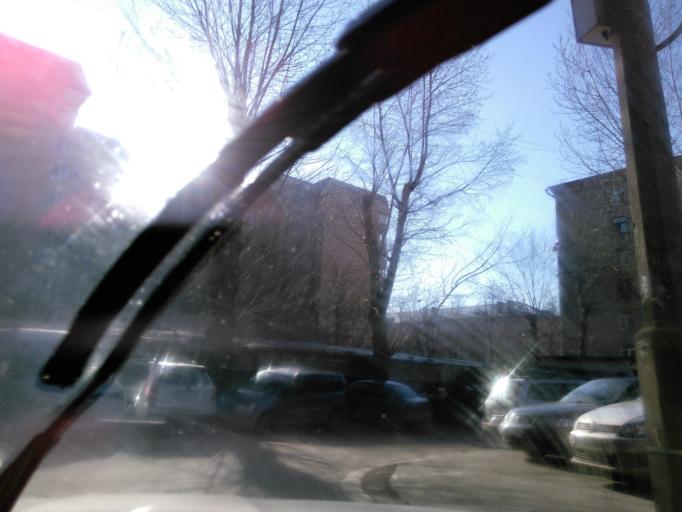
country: RU
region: Moskovskaya
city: Koptevo
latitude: 55.8173
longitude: 37.5240
